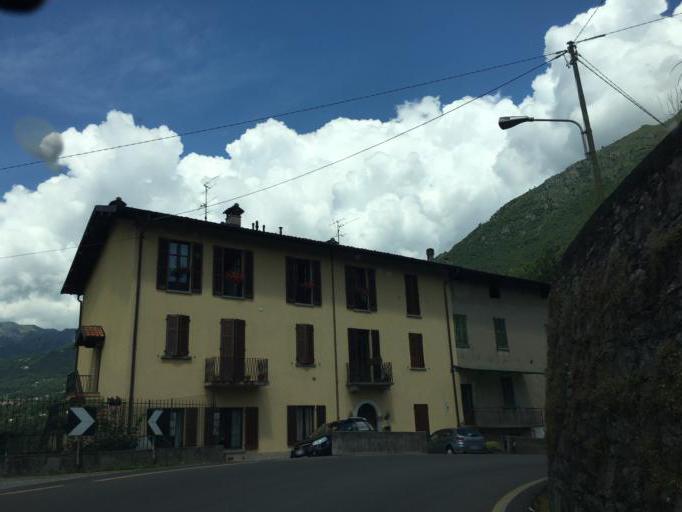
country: IT
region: Lombardy
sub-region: Provincia di Como
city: Carlazzo
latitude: 46.0401
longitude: 9.1737
